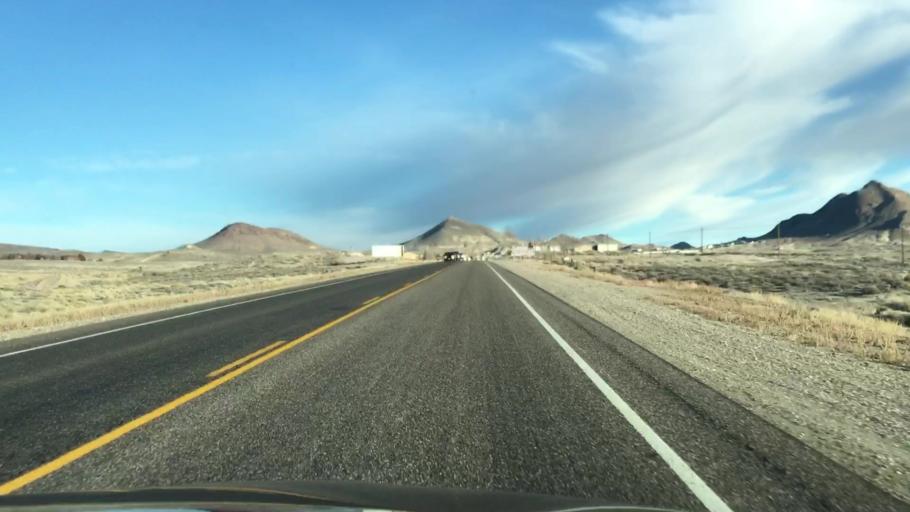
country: US
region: Nevada
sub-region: Nye County
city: Tonopah
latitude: 38.0808
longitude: -117.2643
